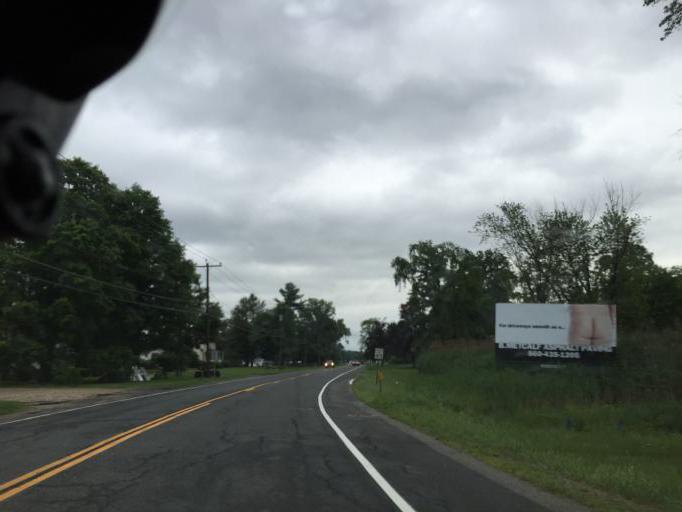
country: US
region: Connecticut
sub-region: Litchfield County
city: Canaan
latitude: 42.0384
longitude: -73.3258
